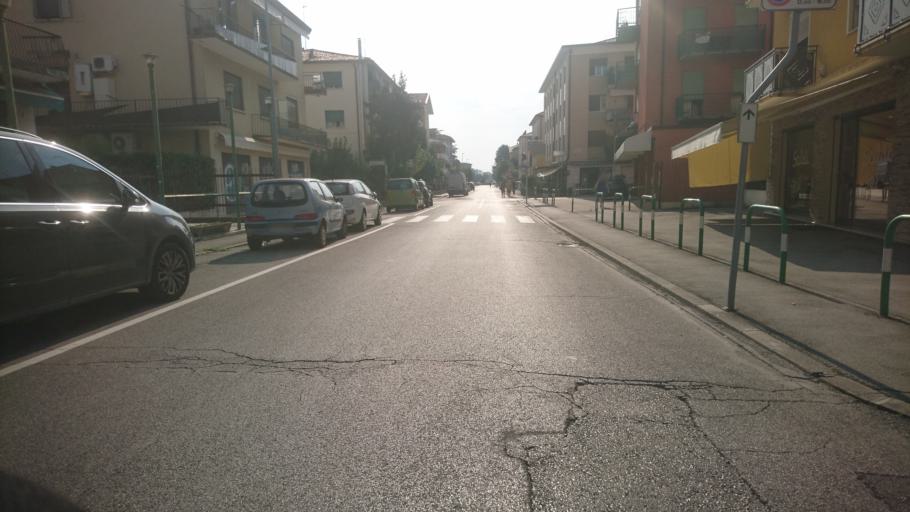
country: IT
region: Veneto
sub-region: Provincia di Padova
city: Padova
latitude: 45.4314
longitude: 11.8914
